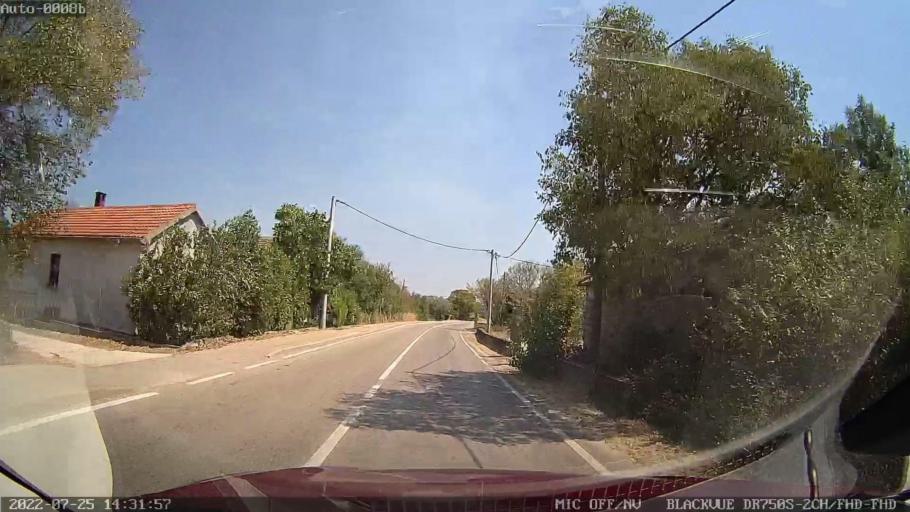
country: HR
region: Zadarska
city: Galovac
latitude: 44.1083
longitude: 15.3763
